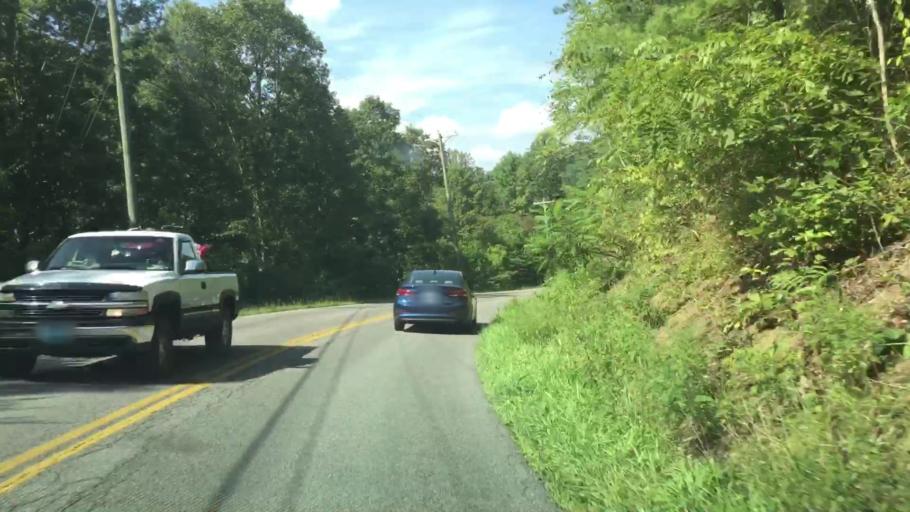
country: US
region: Tennessee
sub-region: Sullivan County
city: Fairmount
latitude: 36.6054
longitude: -82.0741
